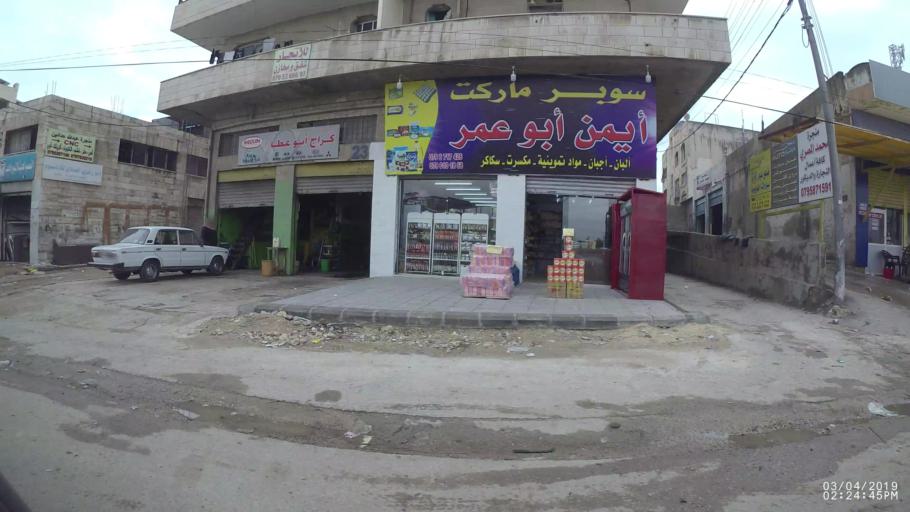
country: JO
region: Amman
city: Wadi as Sir
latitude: 31.9450
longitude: 35.8347
